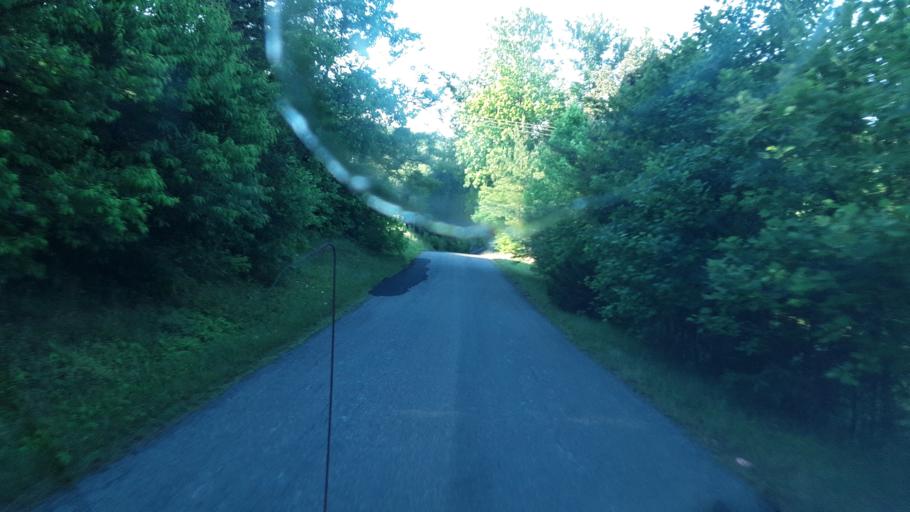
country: US
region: Virginia
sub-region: Pittsylvania County
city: Chatham
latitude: 36.8496
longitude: -79.4513
